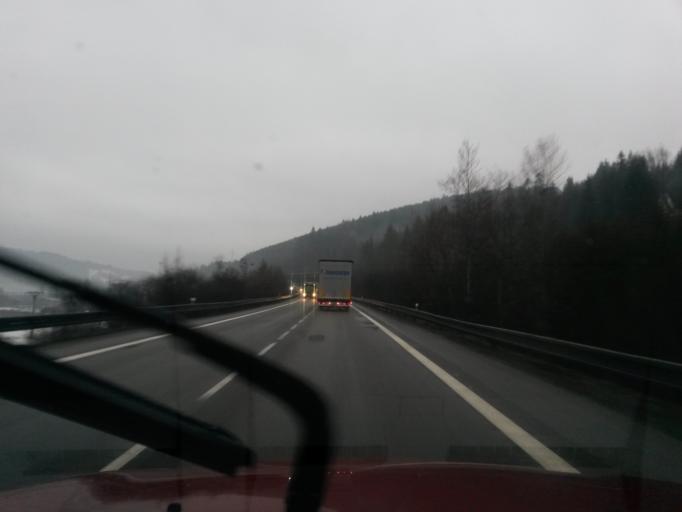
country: SK
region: Zilinsky
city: Cadca
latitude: 49.3769
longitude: 18.8411
